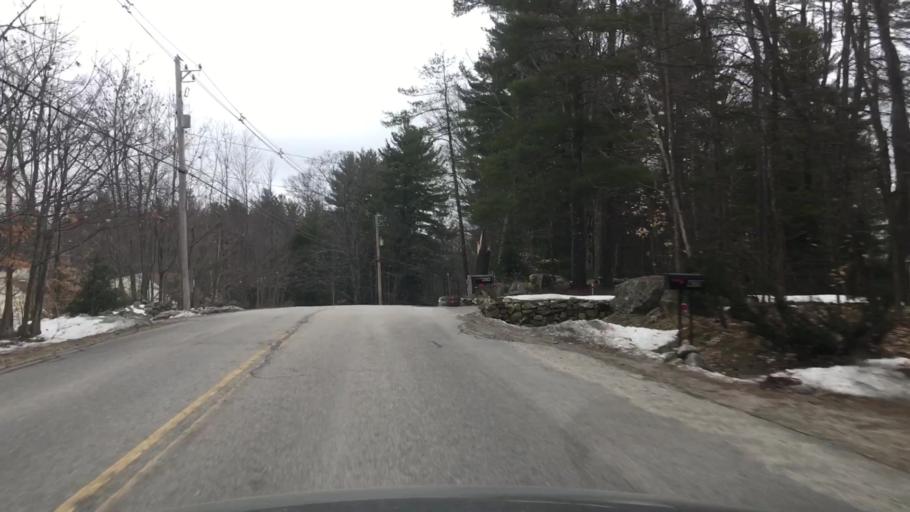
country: US
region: New Hampshire
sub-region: Hillsborough County
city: Goffstown
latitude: 42.9762
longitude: -71.6367
